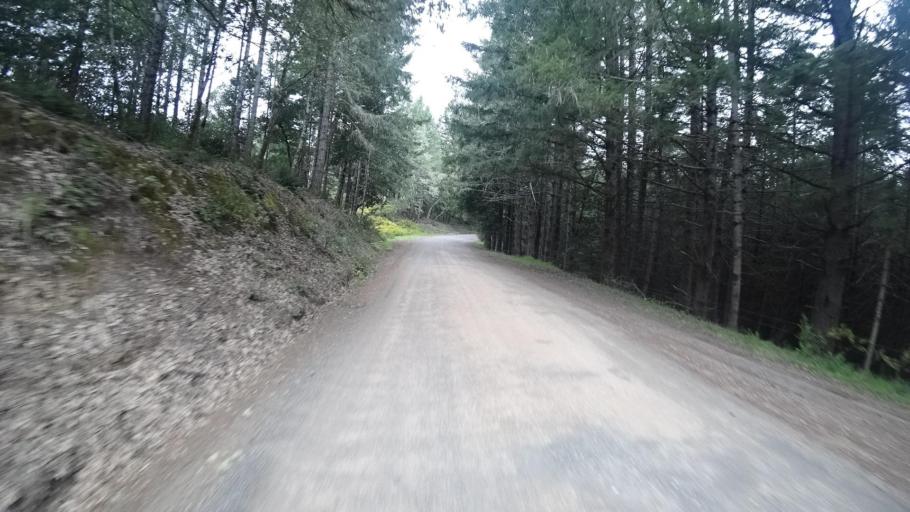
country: US
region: California
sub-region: Humboldt County
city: Redway
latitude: 40.2427
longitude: -123.7653
